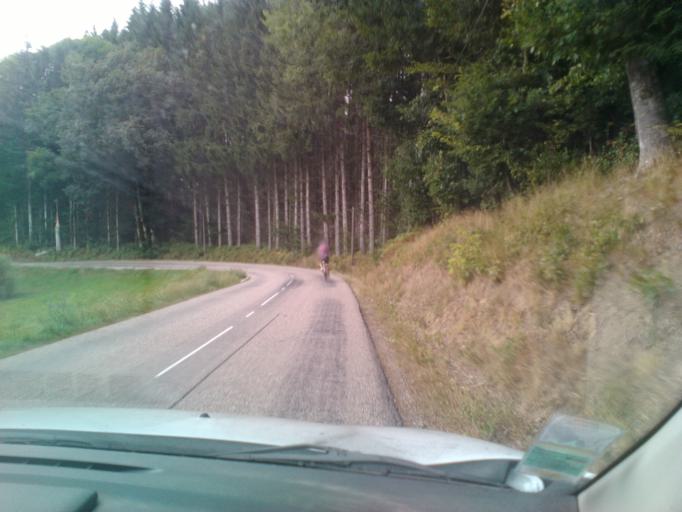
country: FR
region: Lorraine
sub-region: Departement des Vosges
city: Le Tholy
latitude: 48.1137
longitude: 6.7444
